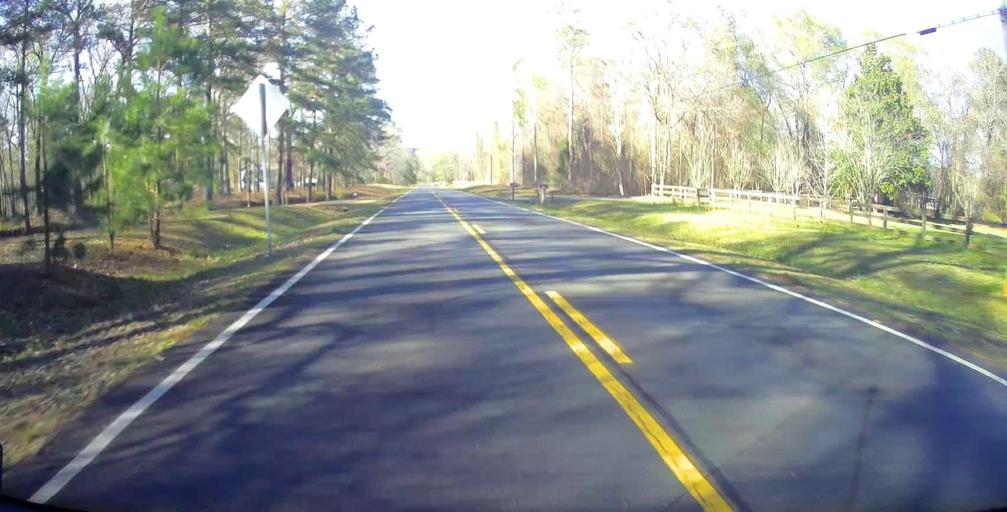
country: US
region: Georgia
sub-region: Peach County
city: Fort Valley
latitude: 32.5141
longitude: -83.9196
